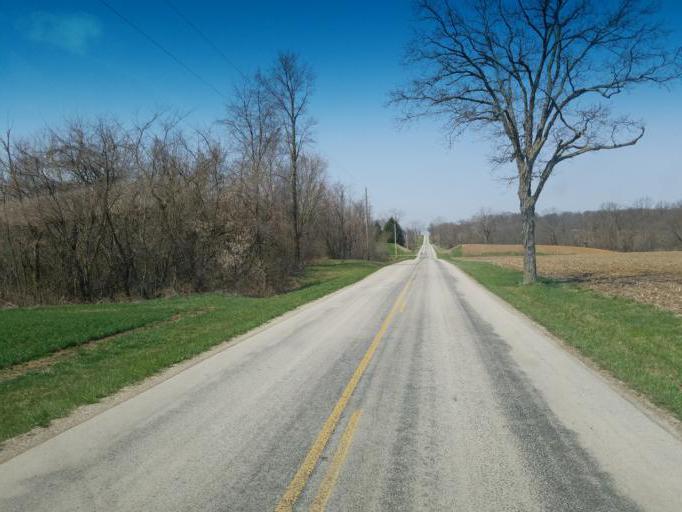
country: US
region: Ohio
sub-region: Wyandot County
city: Upper Sandusky
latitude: 40.8765
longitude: -83.2349
